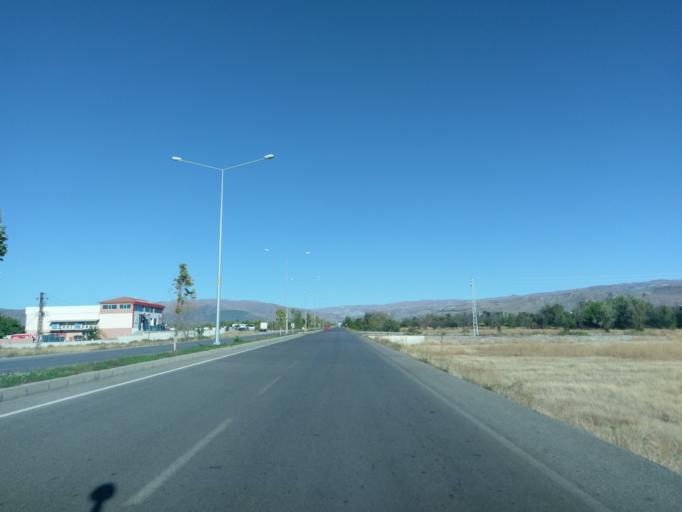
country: TR
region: Erzincan
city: Erzincan
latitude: 39.7759
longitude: 39.4169
